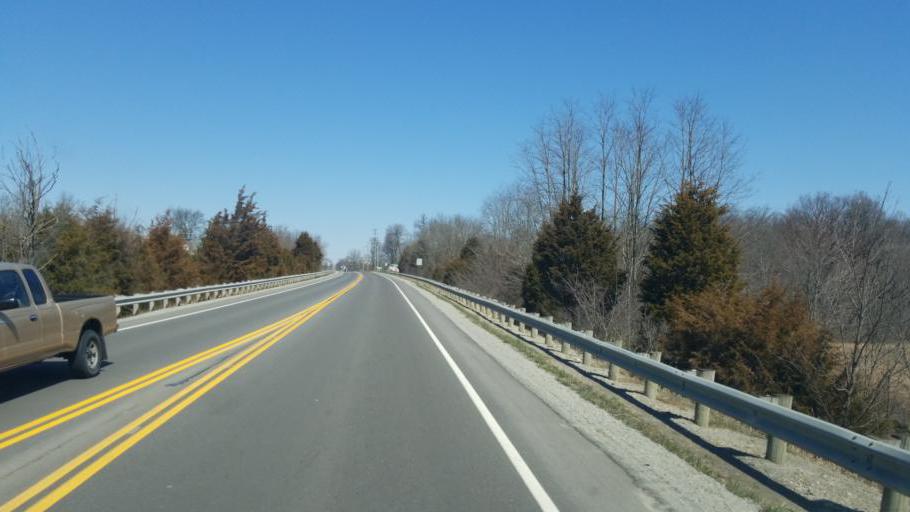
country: US
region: Ohio
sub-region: Highland County
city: Hillsboro
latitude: 39.1904
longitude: -83.6146
